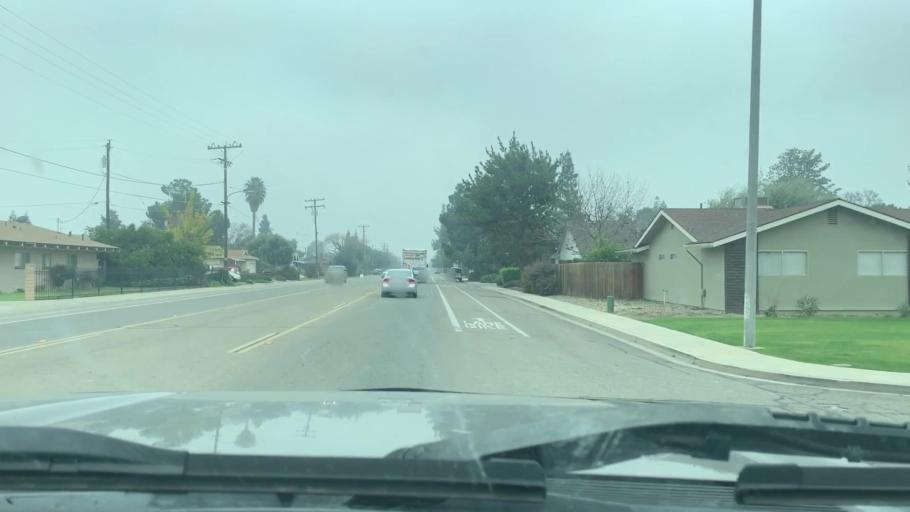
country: US
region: California
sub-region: Tulare County
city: Visalia
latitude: 36.3107
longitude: -119.3228
